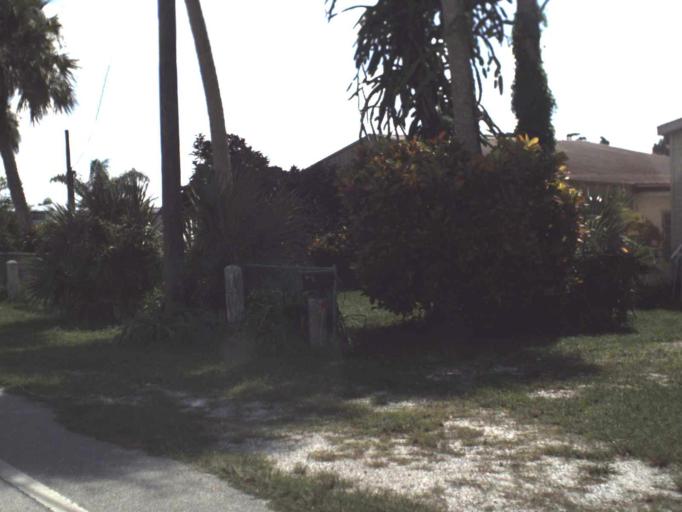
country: US
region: Florida
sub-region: Okeechobee County
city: Taylor Creek
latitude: 27.1919
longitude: -80.7574
